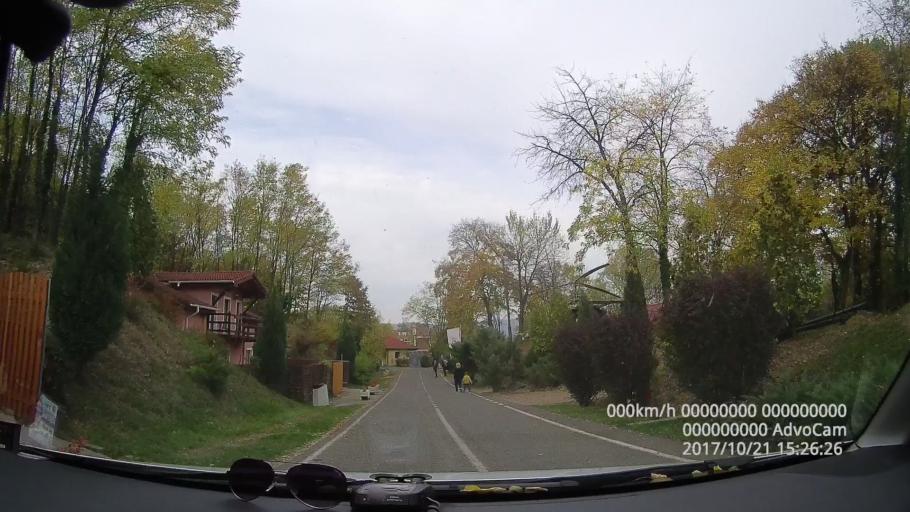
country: RO
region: Hunedoara
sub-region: Municipiul Deva
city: Deva
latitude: 45.8685
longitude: 22.9215
